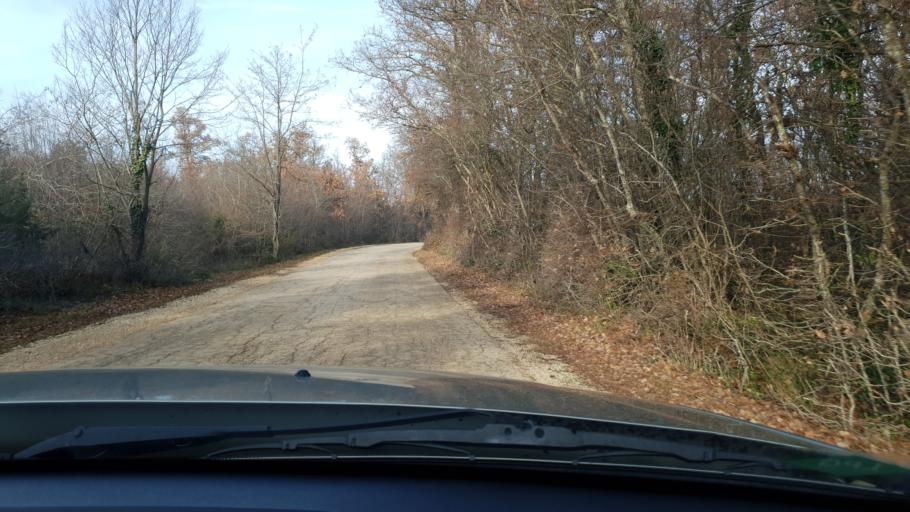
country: HR
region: Istarska
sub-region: Grad Porec
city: Porec
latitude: 45.2500
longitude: 13.6610
